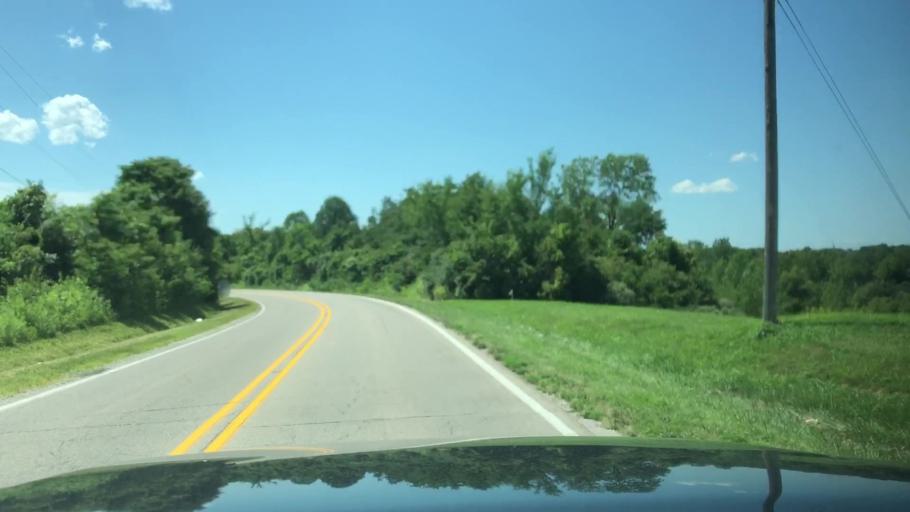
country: US
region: Illinois
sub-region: Saint Clair County
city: Centreville
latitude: 38.5541
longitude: -90.0820
